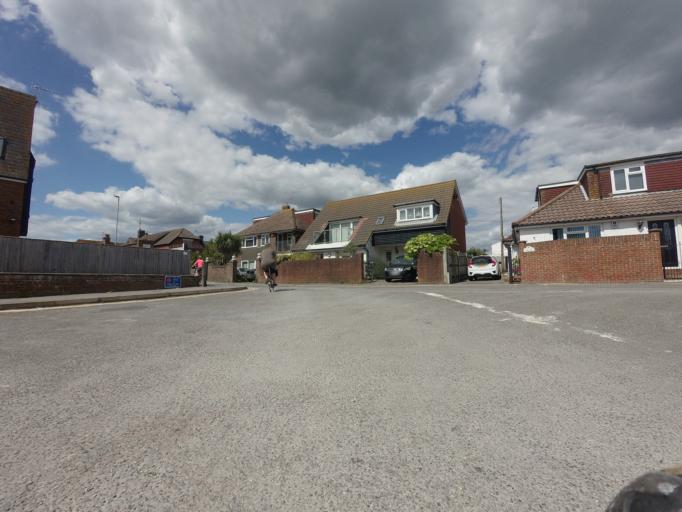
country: GB
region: England
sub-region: East Sussex
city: Pevensey
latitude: 50.8123
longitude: 0.3524
